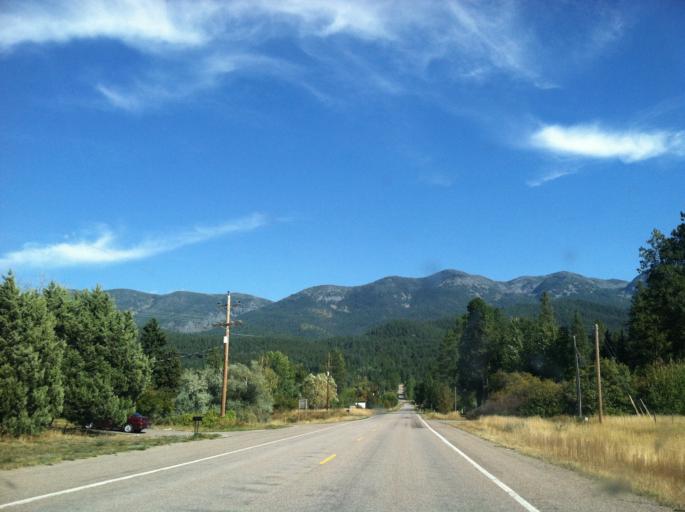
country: US
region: Montana
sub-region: Lake County
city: Polson
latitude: 47.6889
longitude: -114.0666
